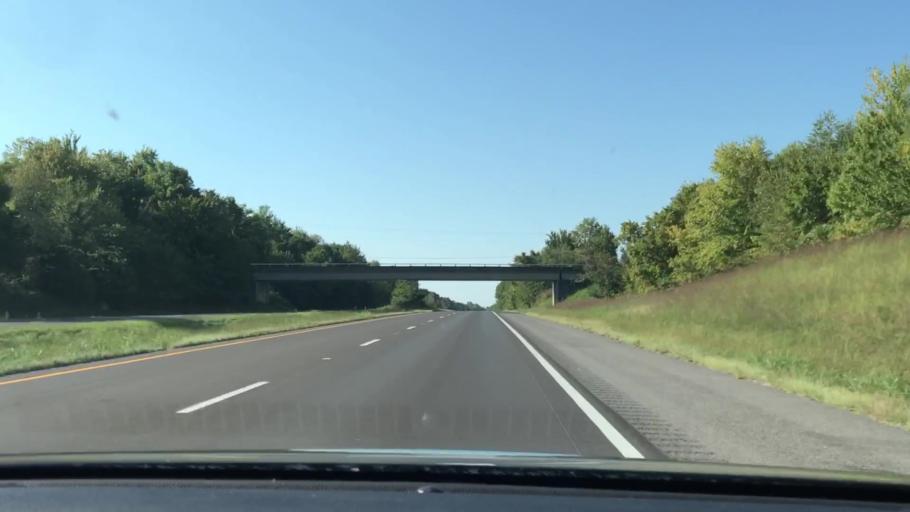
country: US
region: Kentucky
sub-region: Graves County
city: Mayfield
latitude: 36.6678
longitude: -88.7391
